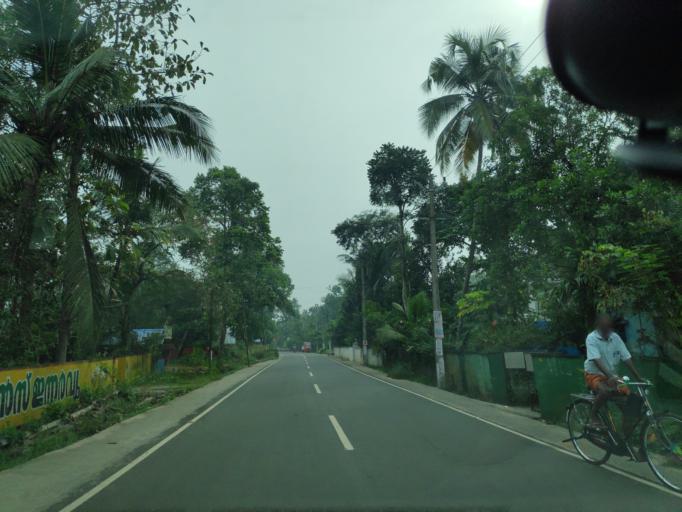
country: IN
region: Kerala
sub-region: Alappuzha
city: Shertallai
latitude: 9.6074
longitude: 76.3503
